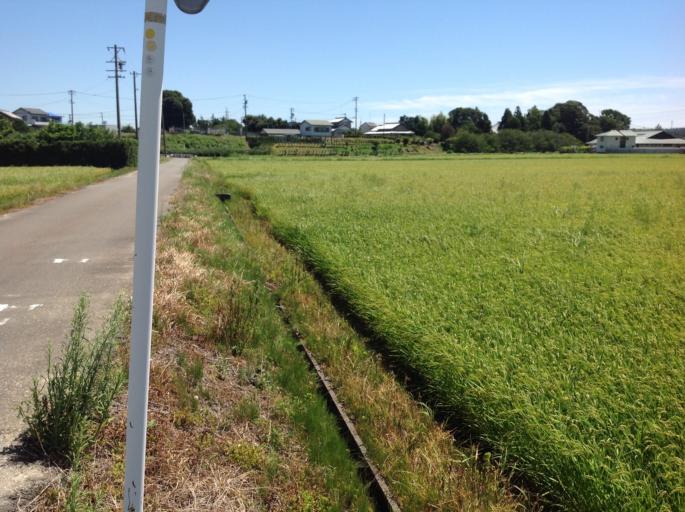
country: JP
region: Shizuoka
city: Kakegawa
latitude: 34.7670
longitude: 137.9671
